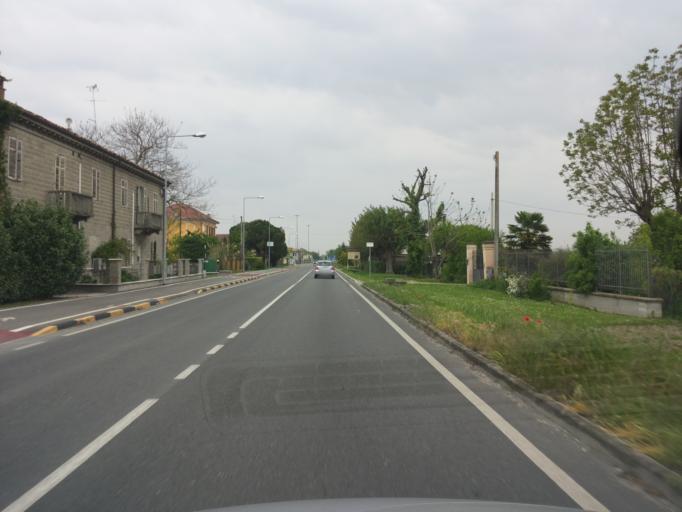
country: IT
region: Piedmont
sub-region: Provincia di Alessandria
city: Casale Monferrato
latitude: 45.1115
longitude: 8.4517
